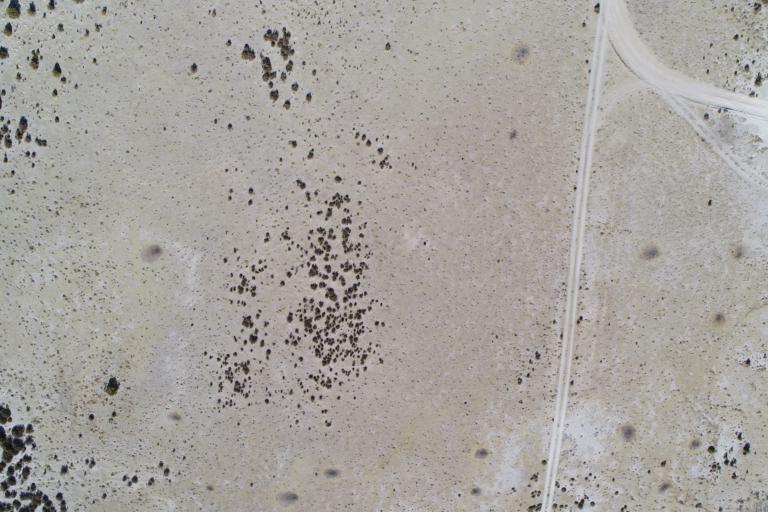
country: BO
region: Potosi
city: Colchani
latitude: -20.3506
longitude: -66.8860
